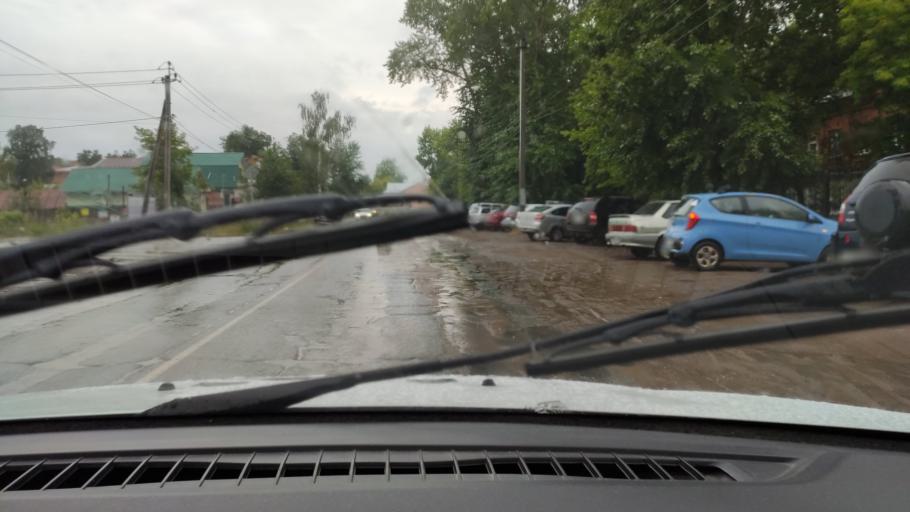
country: RU
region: Udmurtiya
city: Votkinsk
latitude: 57.0651
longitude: 54.0009
